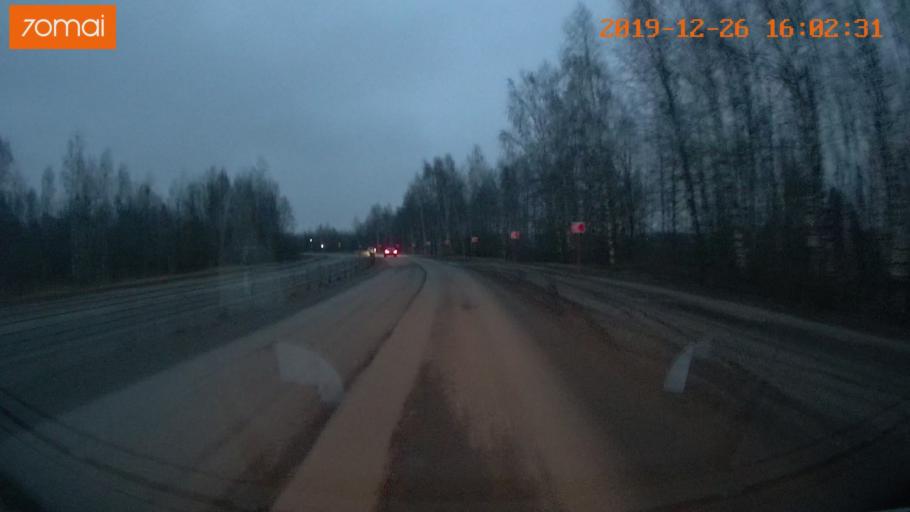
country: RU
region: Jaroslavl
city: Rybinsk
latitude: 58.0111
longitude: 38.8365
